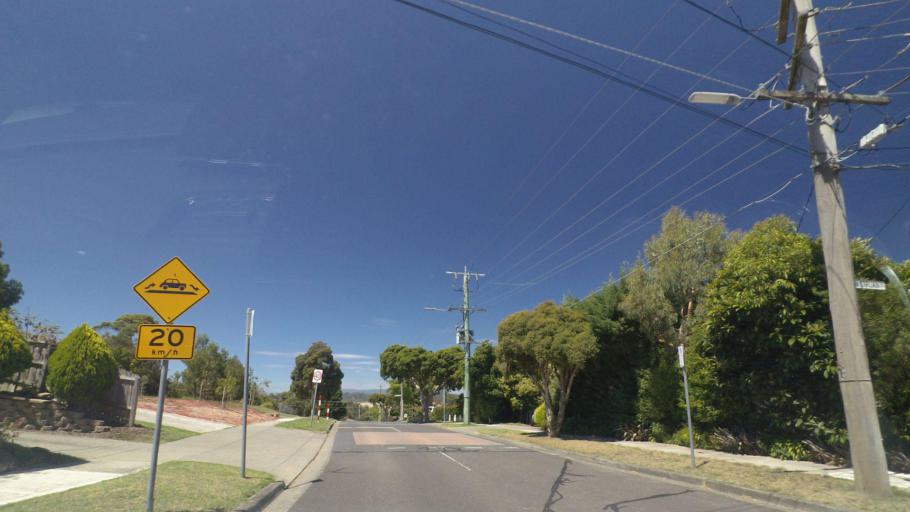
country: AU
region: Victoria
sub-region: Maroondah
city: Croydon North
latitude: -37.7754
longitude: 145.3227
